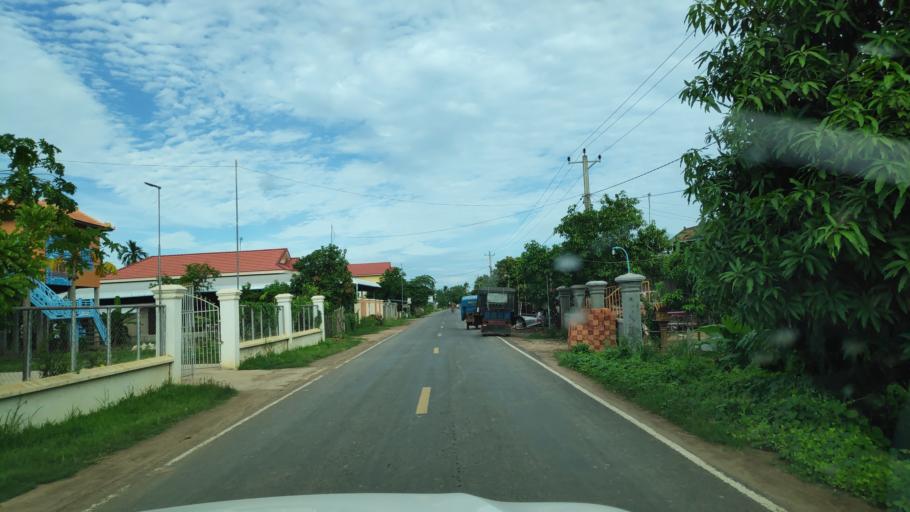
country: KH
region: Kampong Cham
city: Kampong Cham
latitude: 11.9468
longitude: 105.2458
